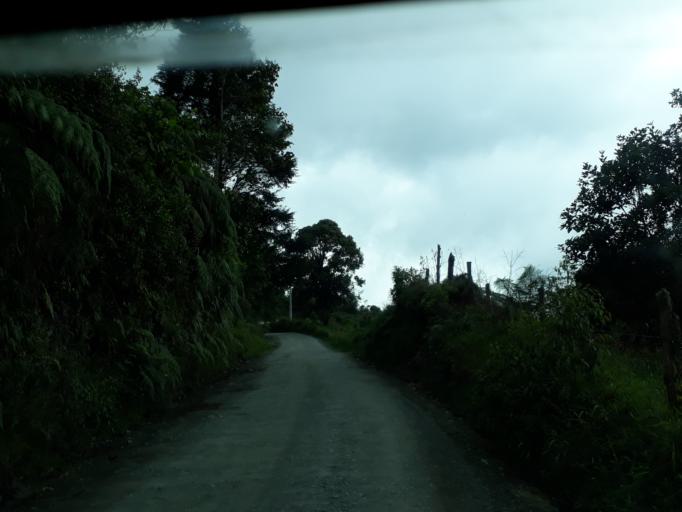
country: CO
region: Cundinamarca
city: Pacho
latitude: 5.2466
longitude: -74.1835
